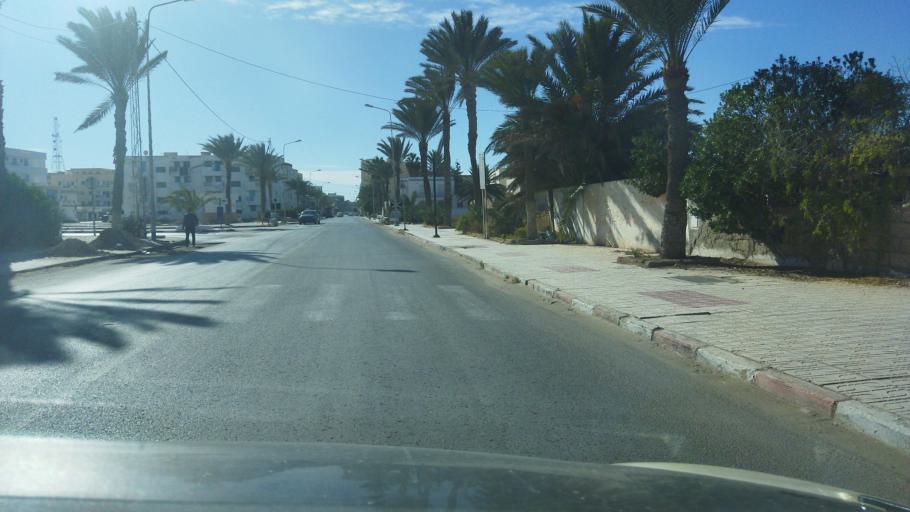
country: TN
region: Qabis
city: Gabes
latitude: 33.8913
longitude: 10.1139
